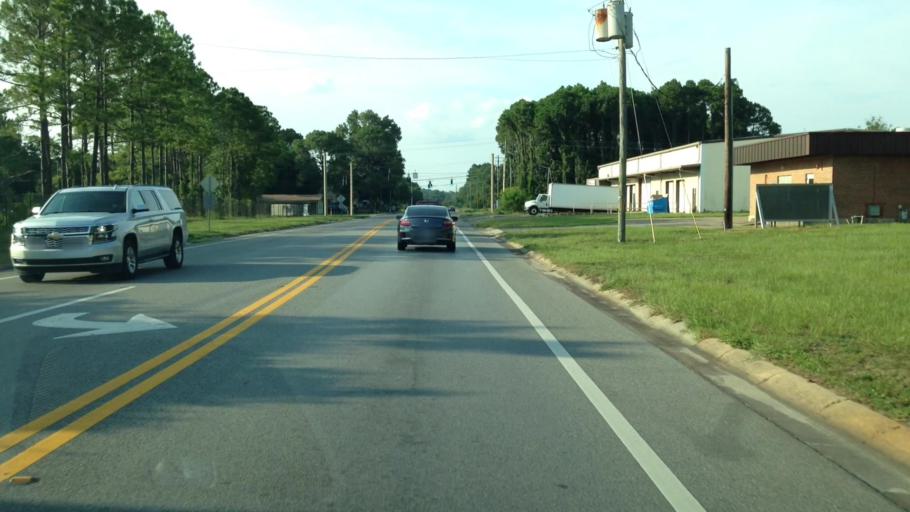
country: US
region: Florida
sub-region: Okaloosa County
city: Mary Esther
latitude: 30.4231
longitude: -86.6673
